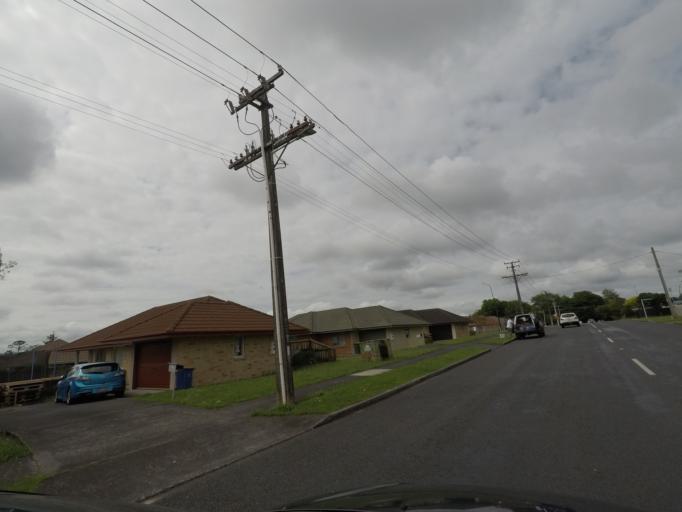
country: NZ
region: Auckland
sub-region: Auckland
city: Waitakere
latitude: -36.9019
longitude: 174.6218
